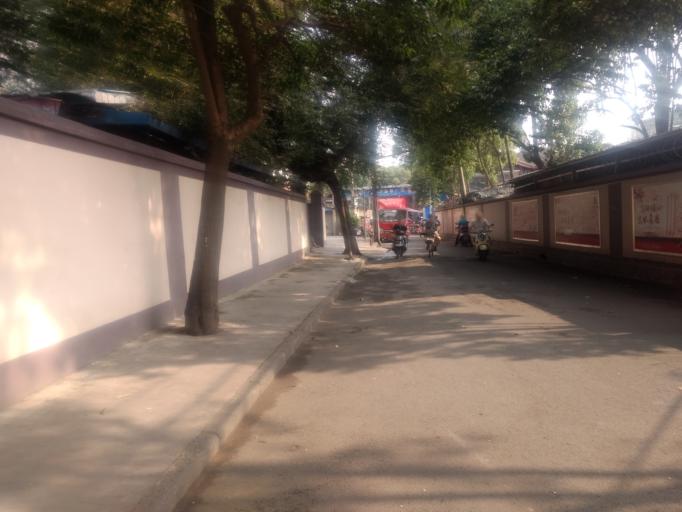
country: CN
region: Sichuan
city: Chengdu
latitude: 30.6756
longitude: 104.0695
